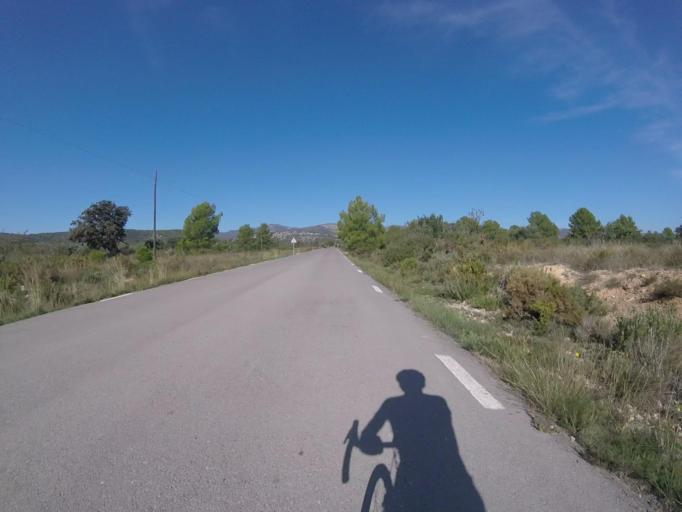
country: ES
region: Valencia
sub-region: Provincia de Castello
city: Sarratella
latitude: 40.2693
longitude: 0.0616
